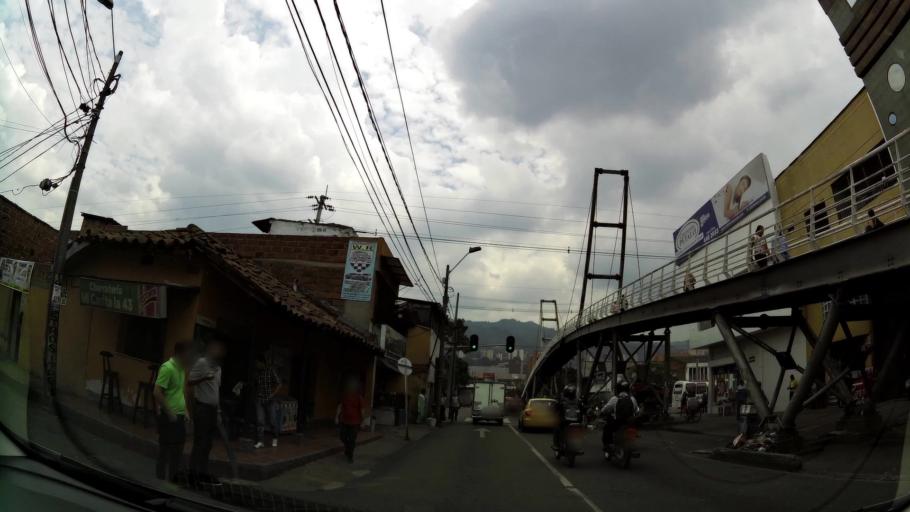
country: CO
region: Antioquia
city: Envigado
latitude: 6.1678
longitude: -75.6077
